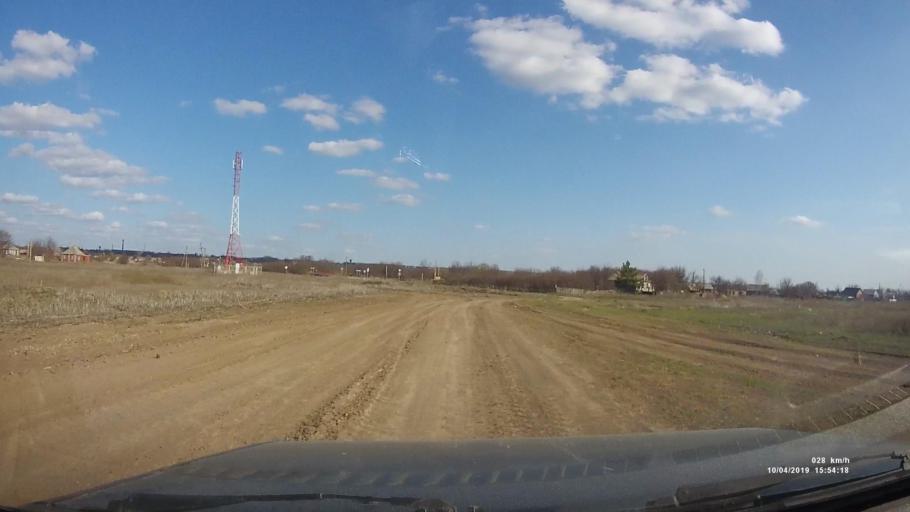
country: RU
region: Rostov
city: Masalovka
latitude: 48.4147
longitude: 40.2594
